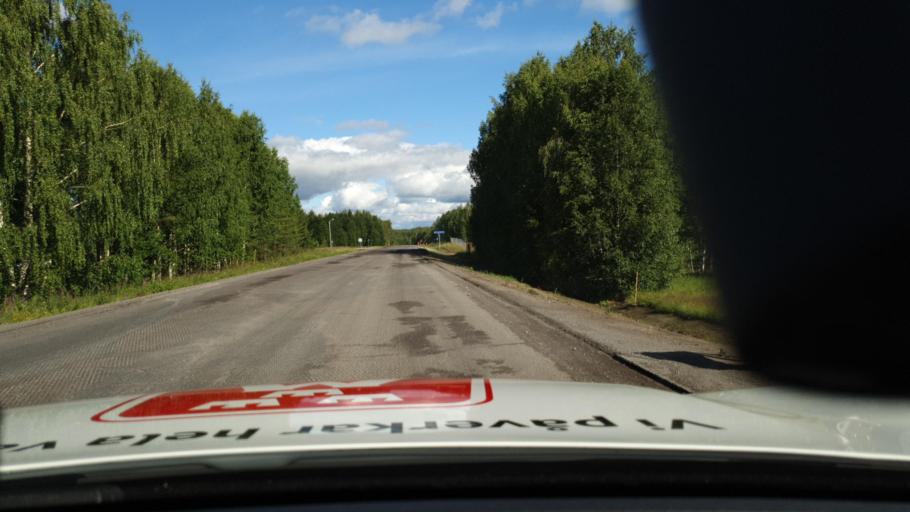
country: SE
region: Norrbotten
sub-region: Bodens Kommun
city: Boden
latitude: 65.8876
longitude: 21.3920
